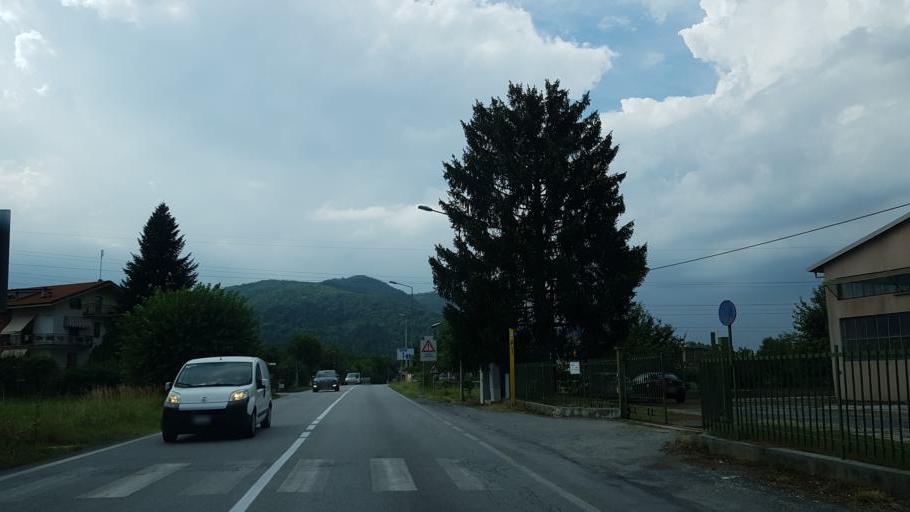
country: IT
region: Piedmont
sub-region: Provincia di Cuneo
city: Borgo San Dalmazzo
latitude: 44.3378
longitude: 7.4787
